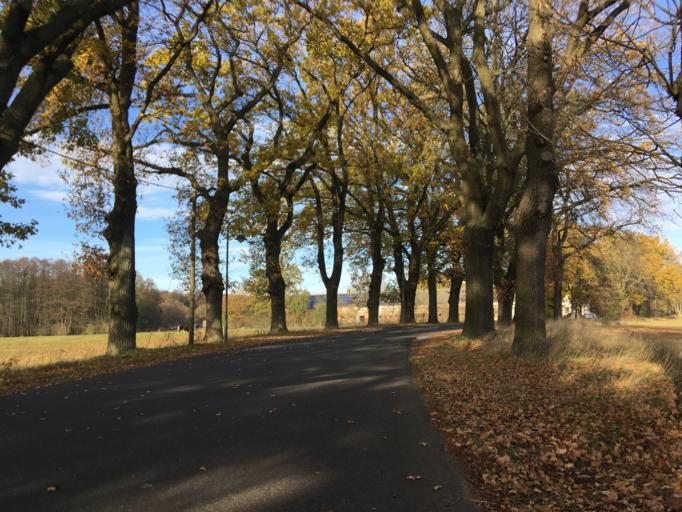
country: DE
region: Brandenburg
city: Gross Koris
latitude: 52.1444
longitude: 13.6792
